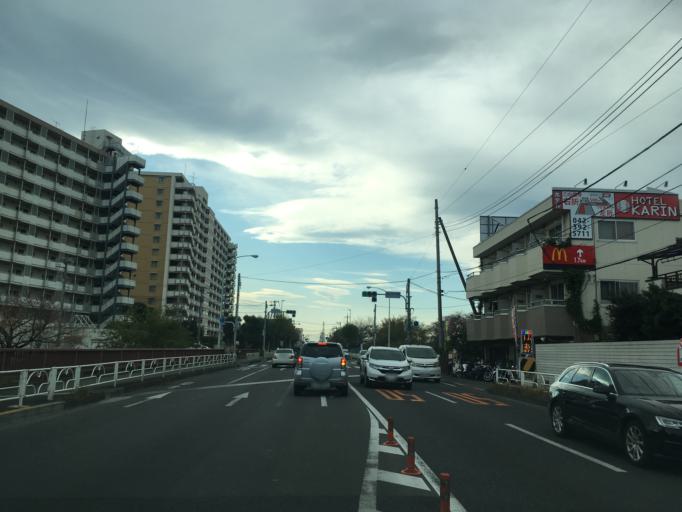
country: JP
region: Tokyo
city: Higashimurayama-shi
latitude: 35.7524
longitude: 139.4628
